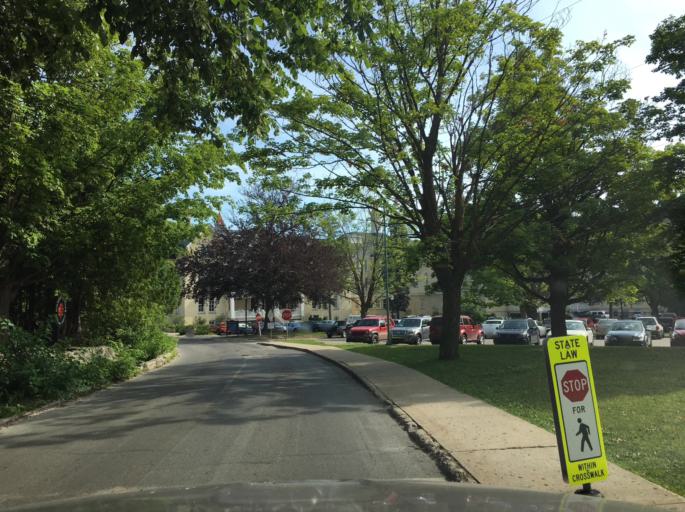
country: US
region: Michigan
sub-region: Grand Traverse County
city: Traverse City
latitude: 44.7562
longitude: -85.6450
